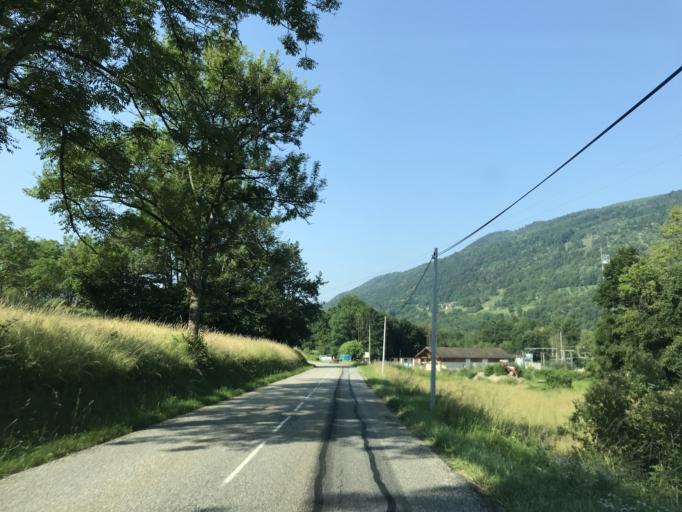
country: FR
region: Rhone-Alpes
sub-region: Departement de la Savoie
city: La Rochette
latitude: 45.4309
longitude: 6.1020
